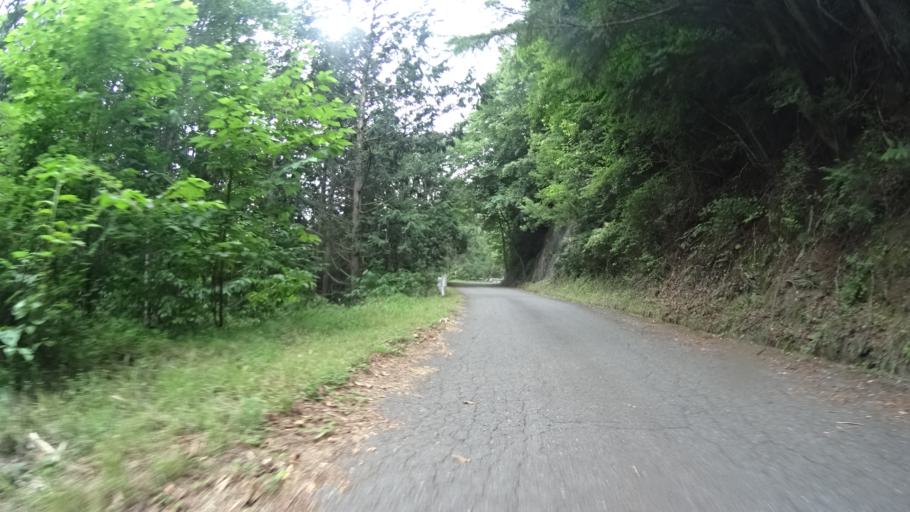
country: JP
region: Yamanashi
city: Kofu-shi
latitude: 35.8137
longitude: 138.5960
